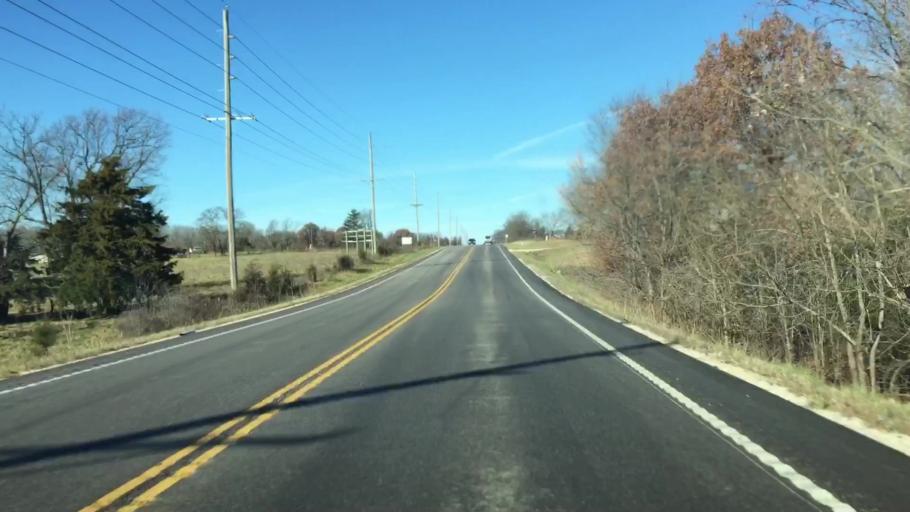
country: US
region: Missouri
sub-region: Miller County
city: Eldon
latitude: 38.3766
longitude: -92.6623
